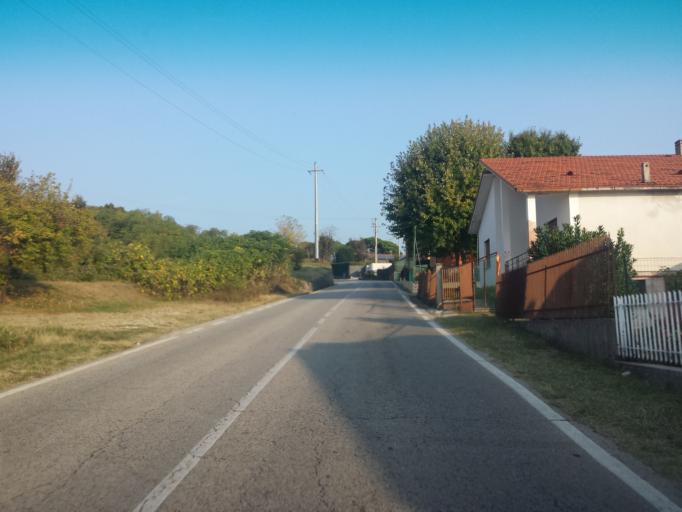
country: IT
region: Veneto
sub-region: Provincia di Vicenza
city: Breganze
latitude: 45.7121
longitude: 11.5757
